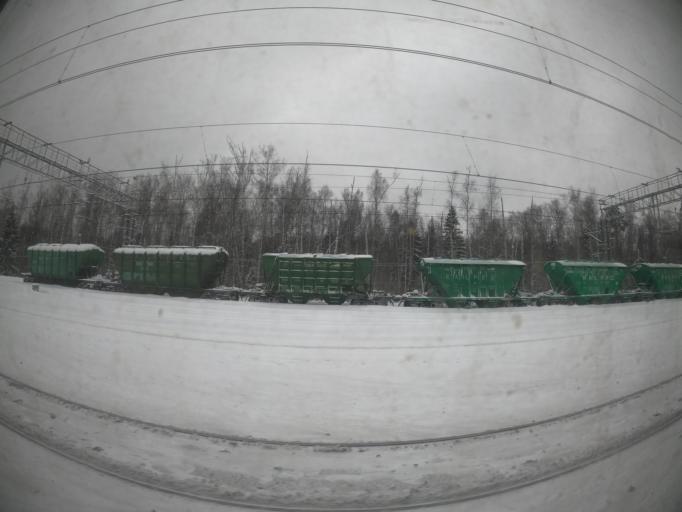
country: RU
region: Moskovskaya
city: Vostryakovo
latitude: 55.4285
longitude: 37.8442
